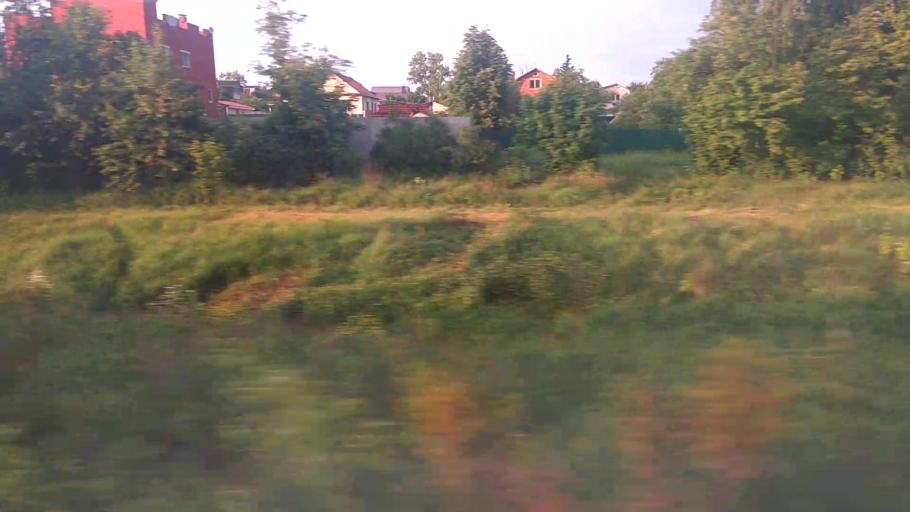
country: RU
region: Moskovskaya
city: Stupino
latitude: 54.8805
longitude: 38.1060
